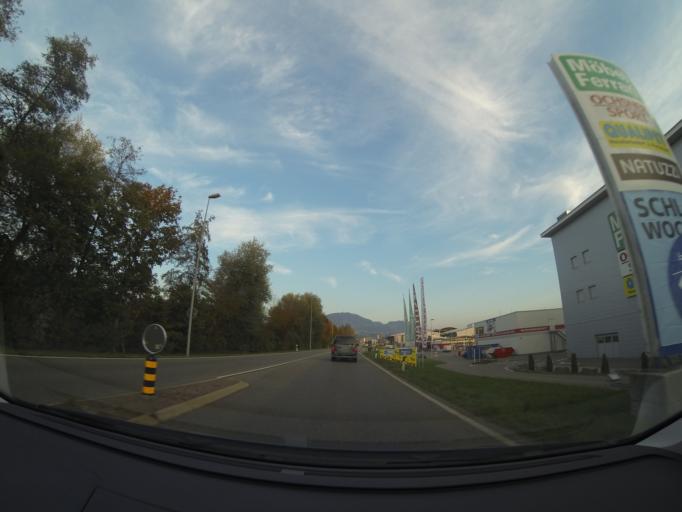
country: CH
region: Zurich
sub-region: Bezirk Hinwil
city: Hinwil
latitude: 47.3063
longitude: 8.8220
